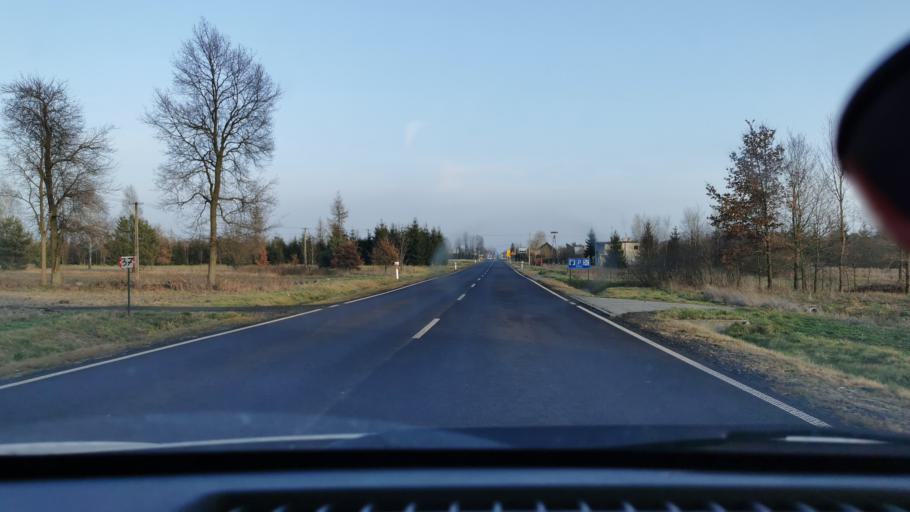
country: PL
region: Lodz Voivodeship
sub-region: Powiat belchatowski
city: Druzbice
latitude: 51.5108
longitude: 19.3664
